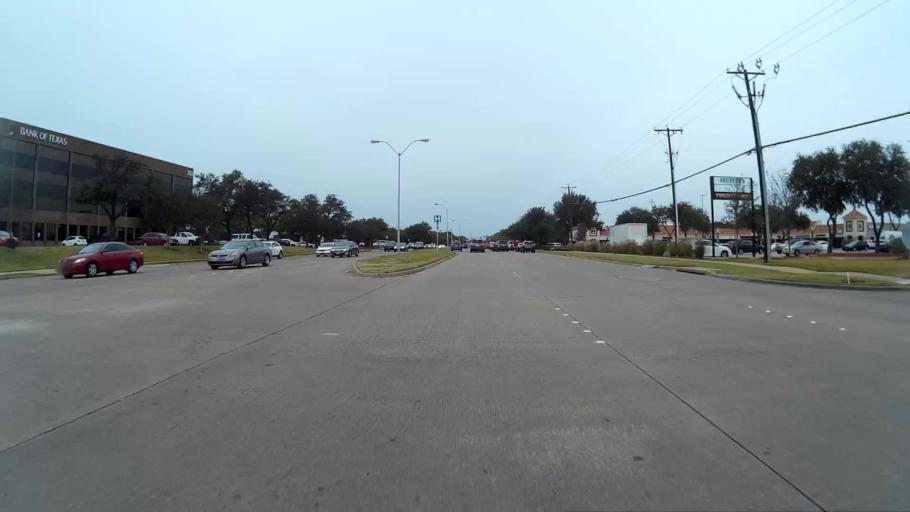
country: US
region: Texas
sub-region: Dallas County
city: Richardson
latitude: 32.9755
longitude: -96.7216
